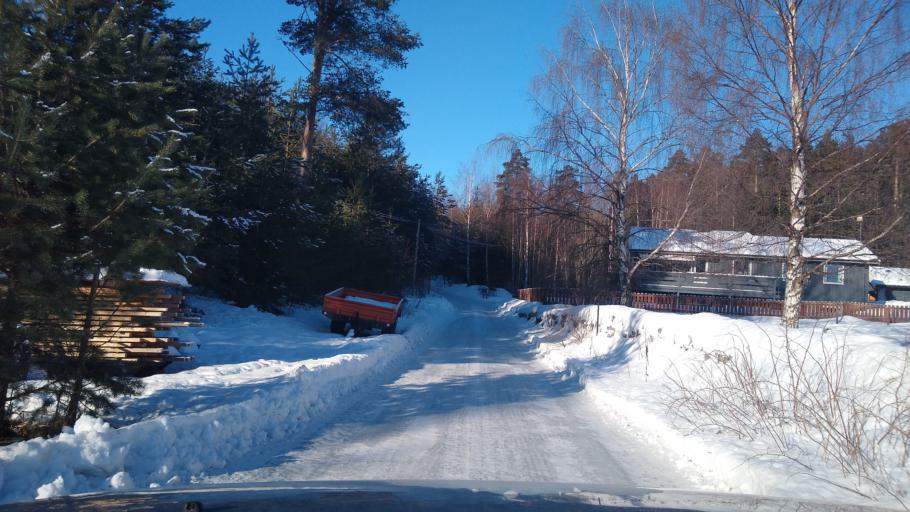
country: NO
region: Oppland
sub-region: Ringebu
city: Ringebu
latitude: 61.5510
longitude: 10.0715
